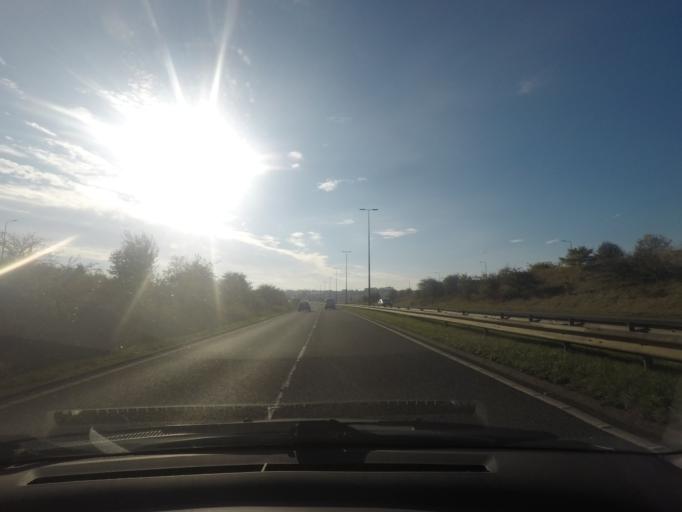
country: GB
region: England
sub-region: North Lincolnshire
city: Barton upon Humber
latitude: 53.6795
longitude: -0.4562
